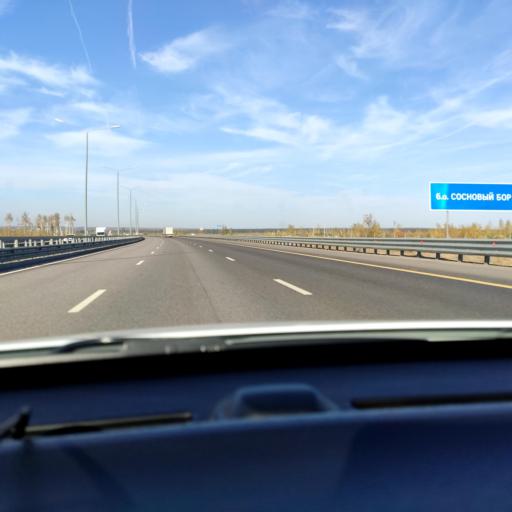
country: RU
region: Voronezj
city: Somovo
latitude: 51.7616
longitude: 39.3059
